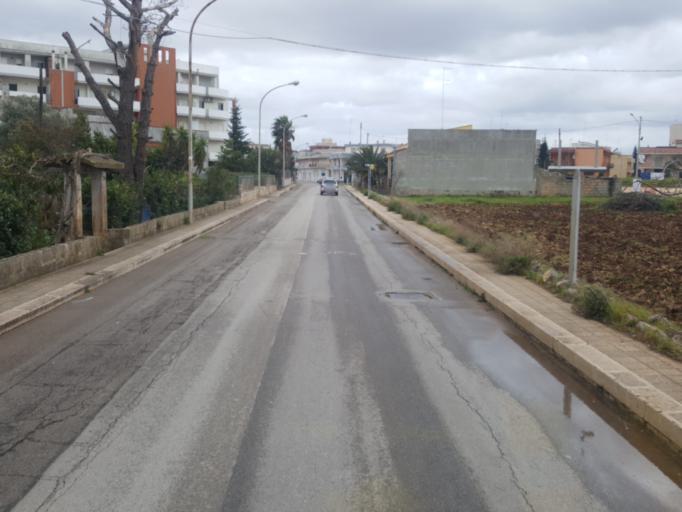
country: IT
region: Apulia
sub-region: Provincia di Bari
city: Turi
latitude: 40.9197
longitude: 17.0298
